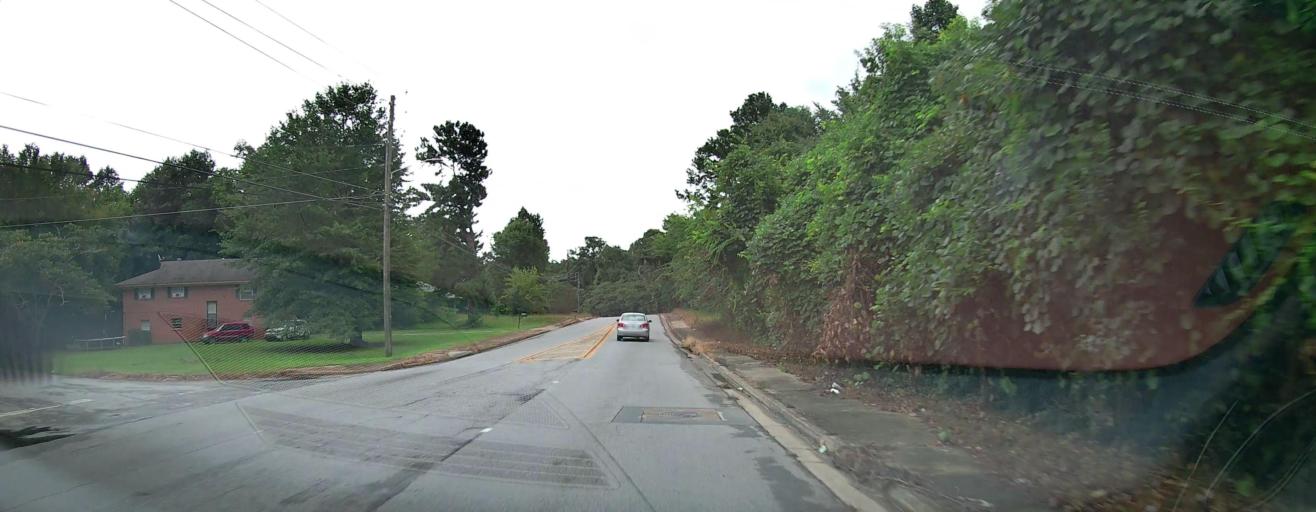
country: US
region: Georgia
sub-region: Bibb County
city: Macon
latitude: 32.7954
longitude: -83.6975
